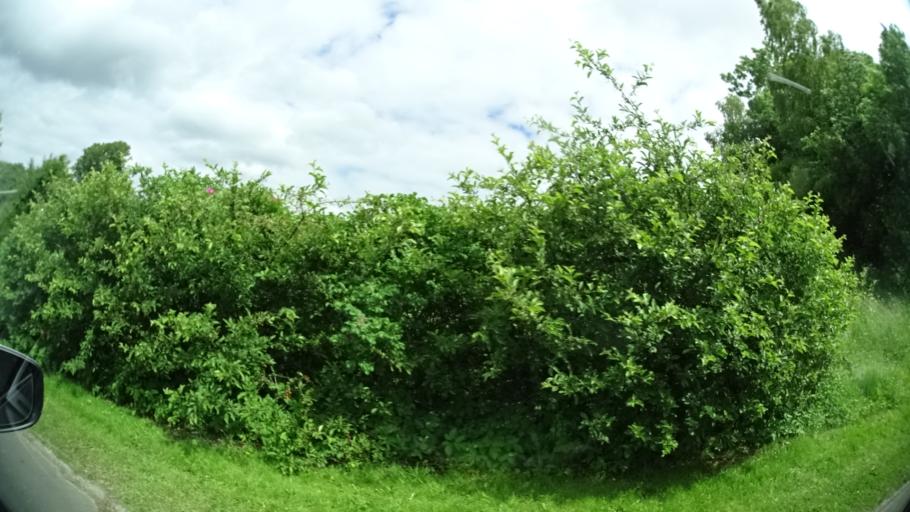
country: DK
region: Central Jutland
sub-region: Syddjurs Kommune
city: Ryomgard
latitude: 56.4041
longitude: 10.5627
